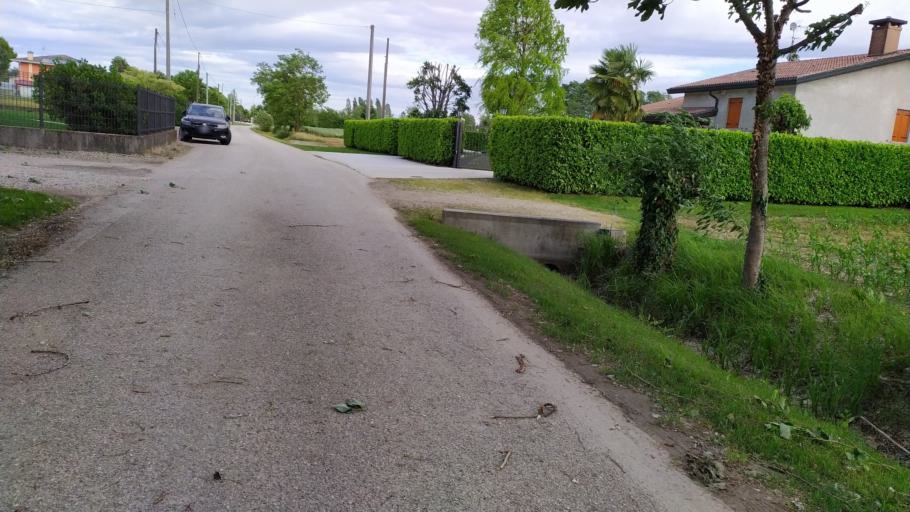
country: IT
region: Veneto
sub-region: Provincia di Padova
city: Villa del Conte
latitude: 45.5916
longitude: 11.8493
